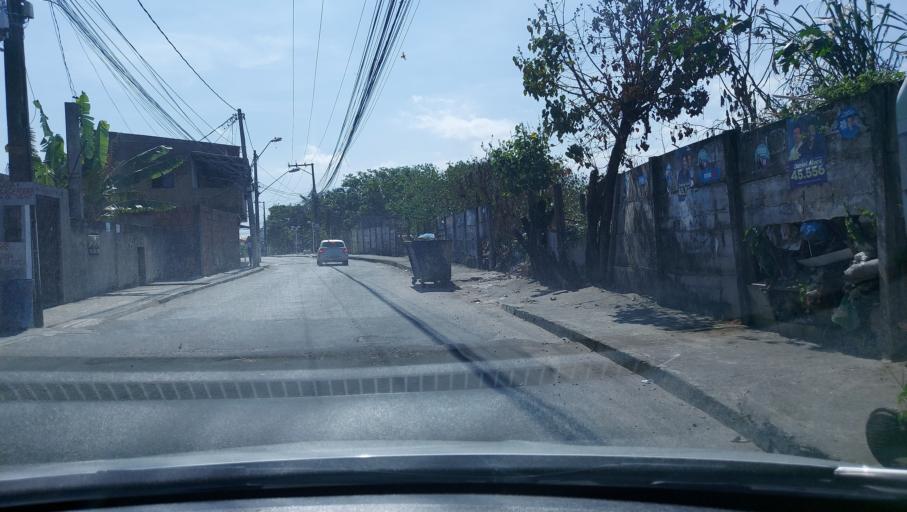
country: BR
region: Bahia
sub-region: Salvador
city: Salvador
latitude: -12.9768
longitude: -38.4391
